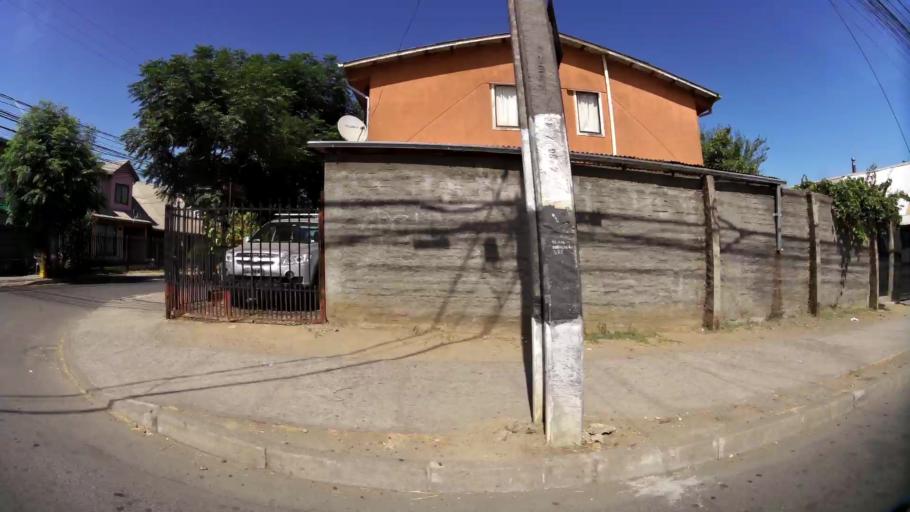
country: CL
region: Maule
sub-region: Provincia de Talca
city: Talca
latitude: -35.4114
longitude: -71.6408
